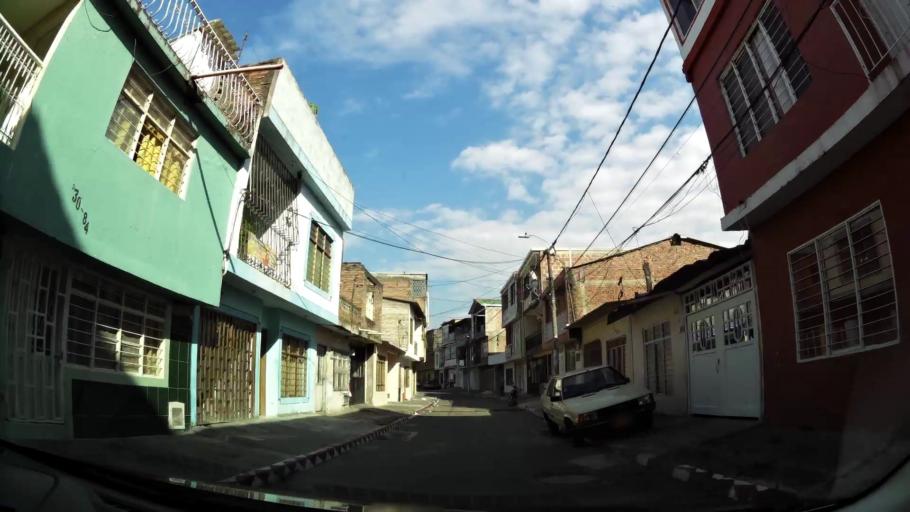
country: CO
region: Valle del Cauca
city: Cali
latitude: 3.4214
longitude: -76.5068
